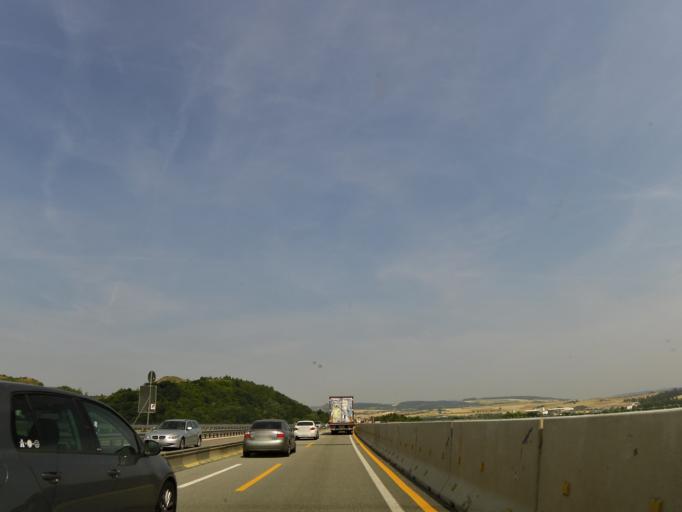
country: DE
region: Rheinland-Pfalz
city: Plaidt
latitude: 50.3816
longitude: 7.3812
